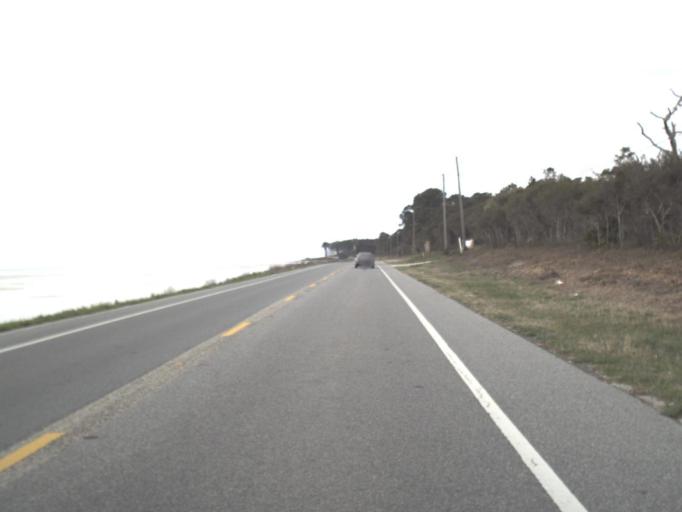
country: US
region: Florida
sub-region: Franklin County
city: Eastpoint
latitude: 29.7770
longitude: -84.7860
